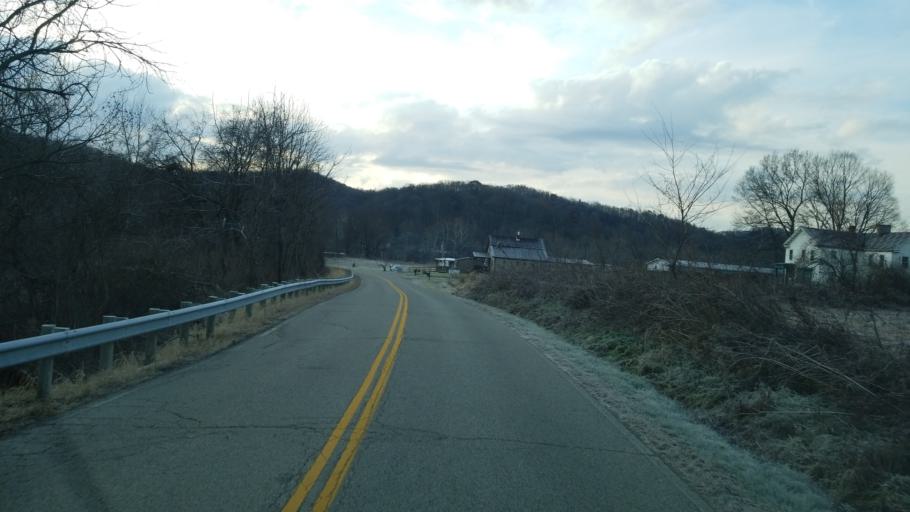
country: US
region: Ohio
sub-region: Ross County
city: Chillicothe
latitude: 39.2370
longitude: -82.8977
